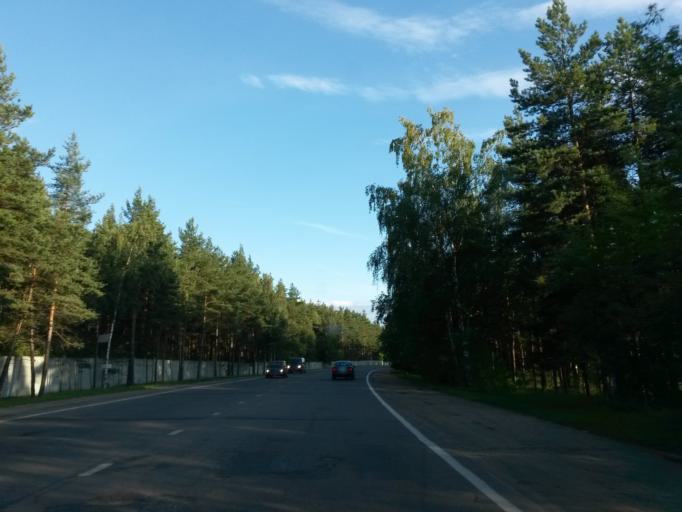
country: RU
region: Jaroslavl
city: Yaroslavl
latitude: 57.6735
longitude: 39.9078
